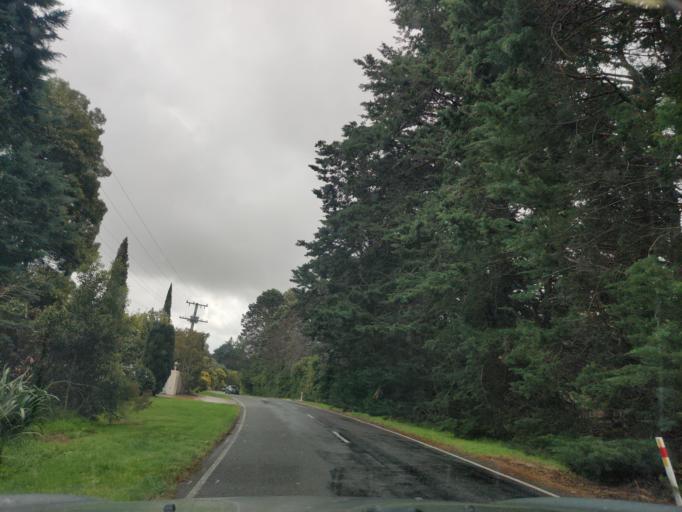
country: NZ
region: Hawke's Bay
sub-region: Hastings District
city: Hastings
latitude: -39.6883
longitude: 176.8989
